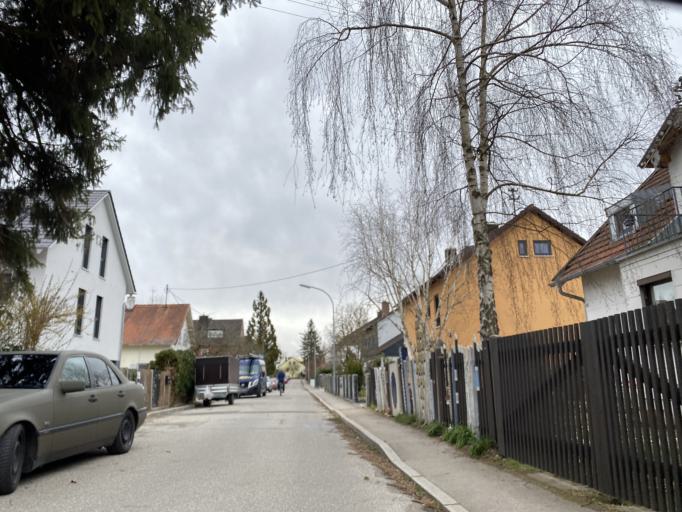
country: DE
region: Bavaria
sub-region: Upper Bavaria
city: Fuerstenfeldbruck
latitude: 48.1866
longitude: 11.2573
